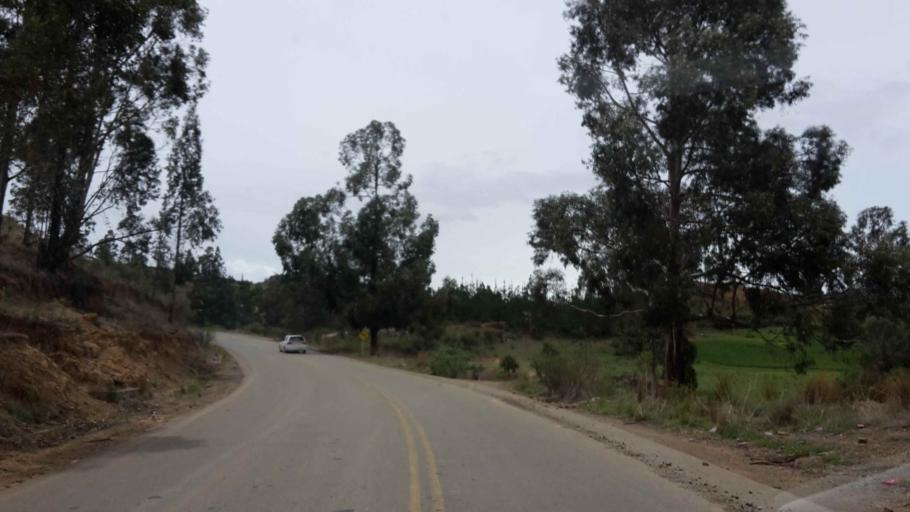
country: BO
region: Cochabamba
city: Totora
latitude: -17.7211
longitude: -65.2003
